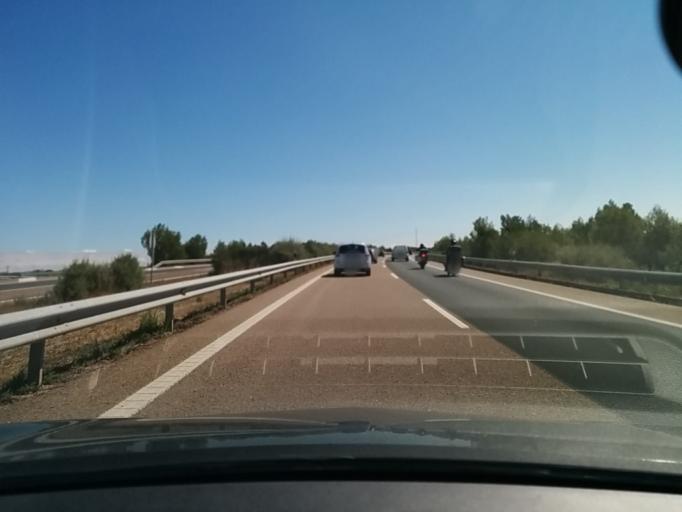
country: ES
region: Aragon
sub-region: Provincia de Huesca
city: Almudebar
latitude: 42.0316
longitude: -0.5884
